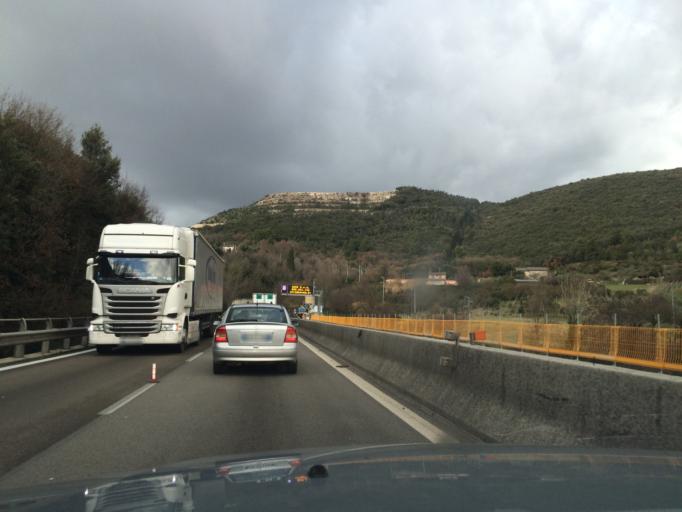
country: IT
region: Umbria
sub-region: Provincia di Terni
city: Narni Scalo
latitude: 42.5422
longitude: 12.4950
